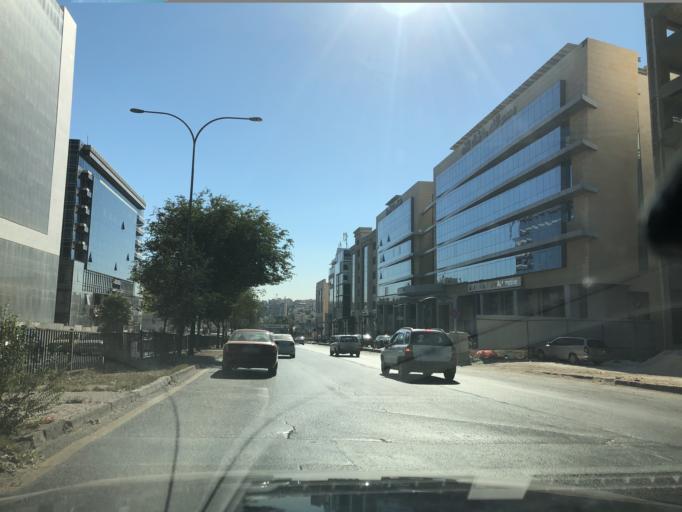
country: JO
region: Amman
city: Wadi as Sir
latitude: 31.9759
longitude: 35.8590
